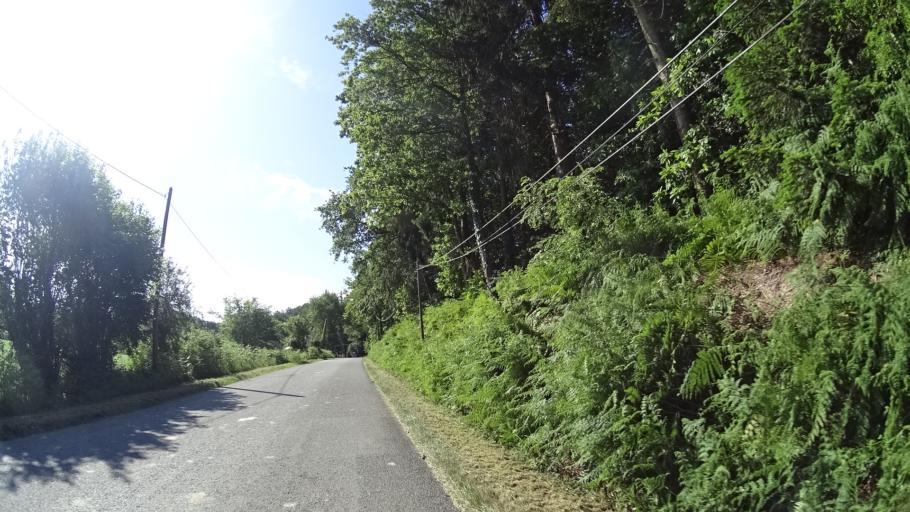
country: FR
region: Brittany
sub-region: Departement d'Ille-et-Vilaine
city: Guipry
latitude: 47.7836
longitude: -1.8518
